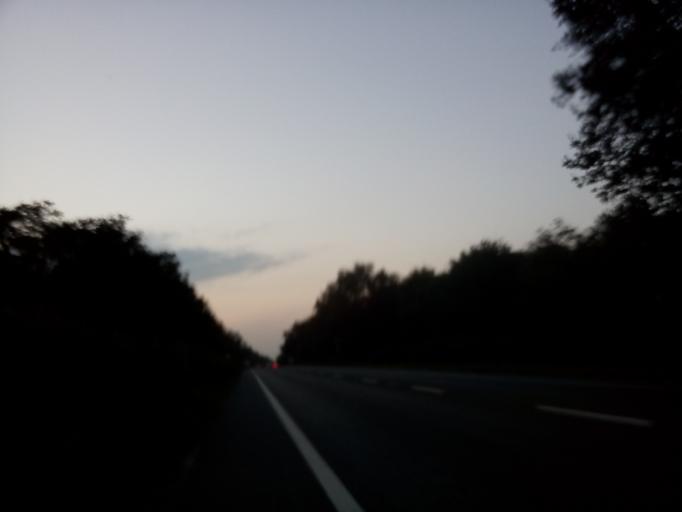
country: GB
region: England
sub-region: Suffolk
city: Kesgrave
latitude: 52.0300
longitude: 1.2230
